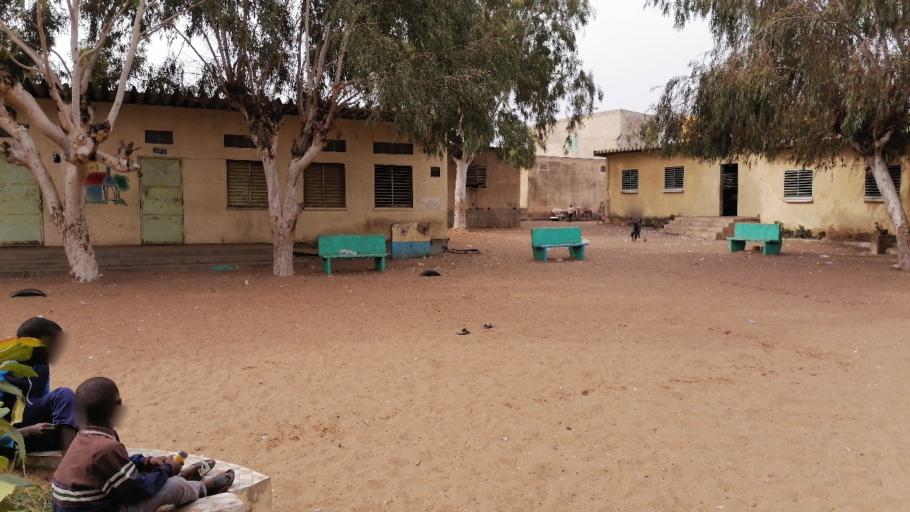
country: SN
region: Dakar
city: Pikine
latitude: 14.7707
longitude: -17.3786
